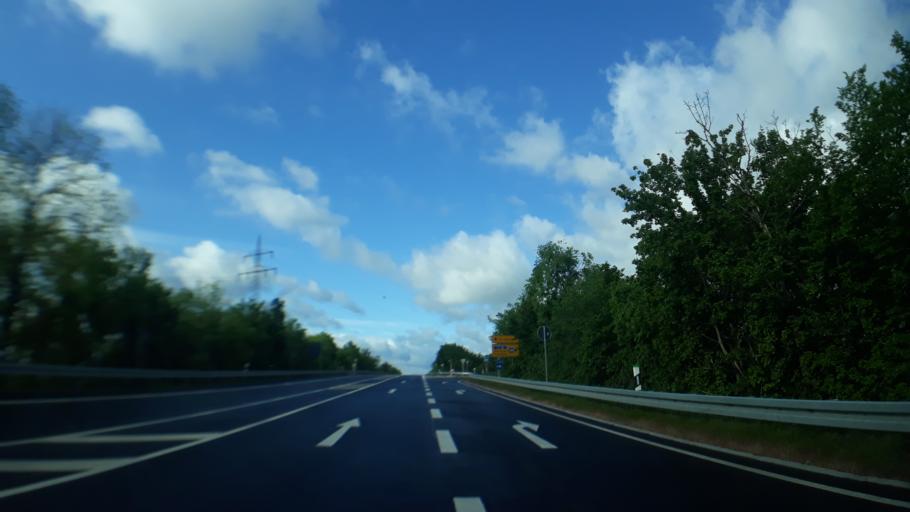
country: DE
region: North Rhine-Westphalia
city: Zulpich
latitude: 50.7135
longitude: 6.6797
